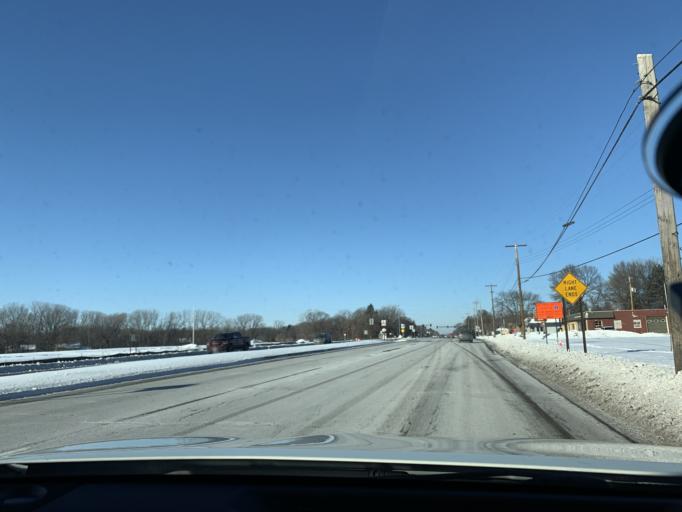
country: US
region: Minnesota
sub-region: Anoka County
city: Coon Rapids
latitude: 45.1533
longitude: -93.3034
